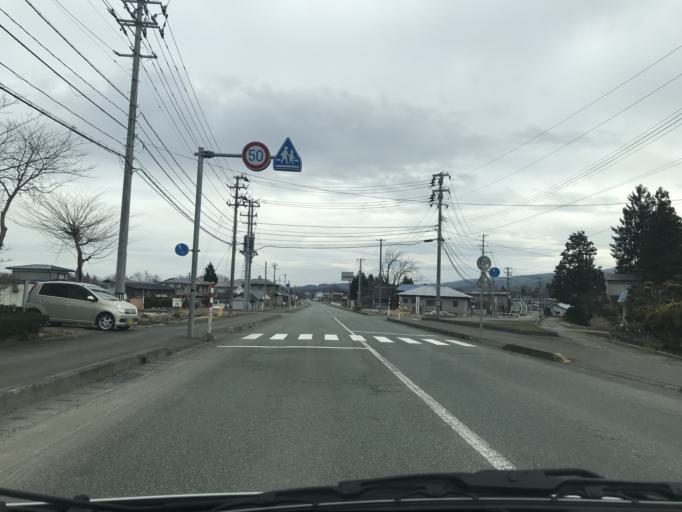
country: JP
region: Iwate
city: Kitakami
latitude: 39.3164
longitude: 140.9747
